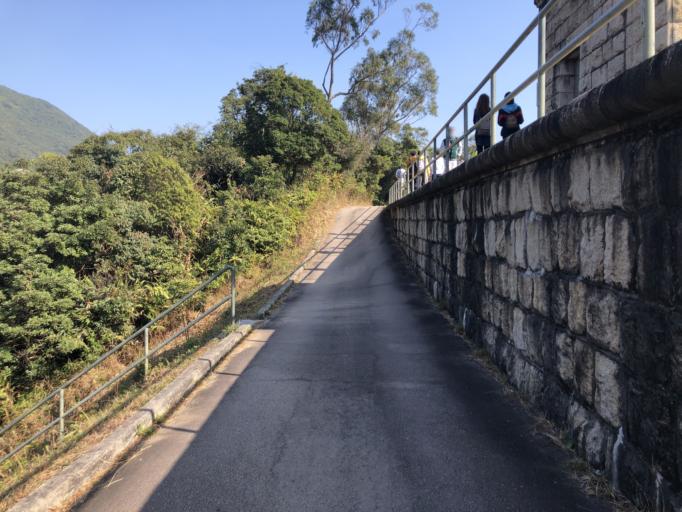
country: HK
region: Wanchai
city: Wan Chai
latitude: 22.2563
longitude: 114.2120
